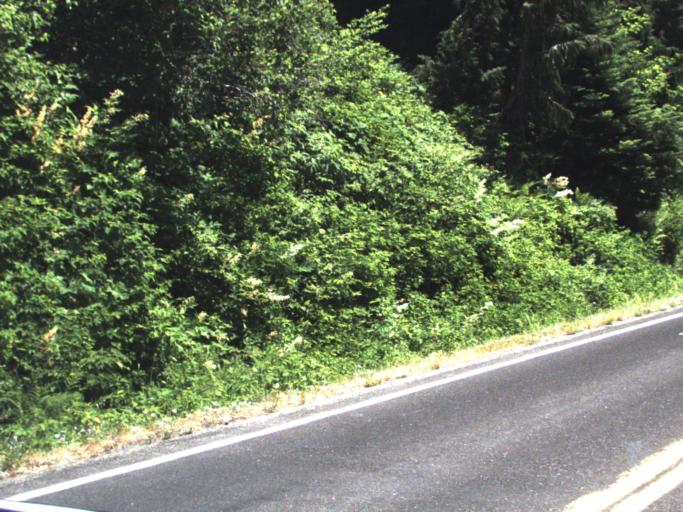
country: US
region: Washington
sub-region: King County
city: Enumclaw
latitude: 46.8574
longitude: -121.5291
